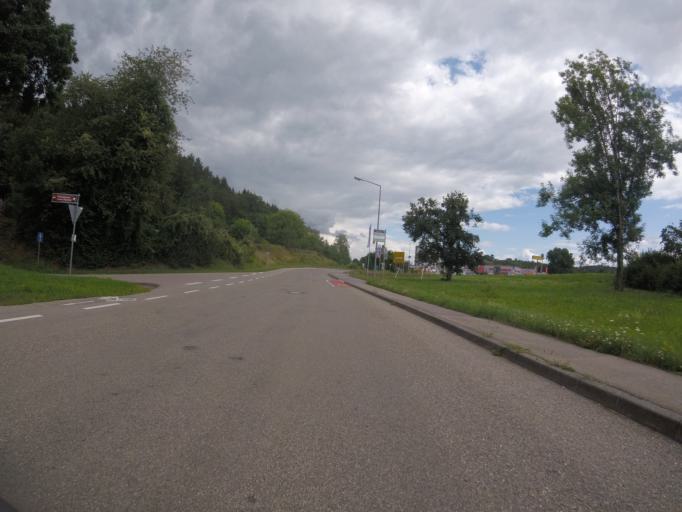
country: DE
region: Baden-Wuerttemberg
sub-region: Regierungsbezirk Stuttgart
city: Schwabisch Gmund
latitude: 48.7892
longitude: 9.7631
